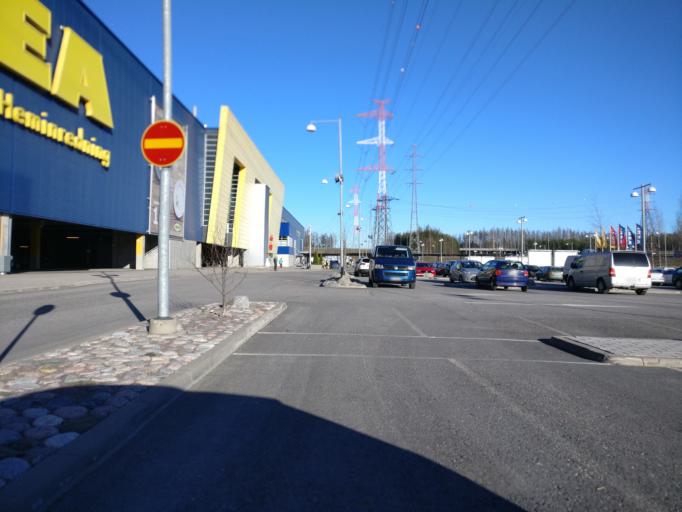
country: FI
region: Uusimaa
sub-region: Helsinki
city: Vantaa
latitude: 60.2768
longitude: 25.0824
